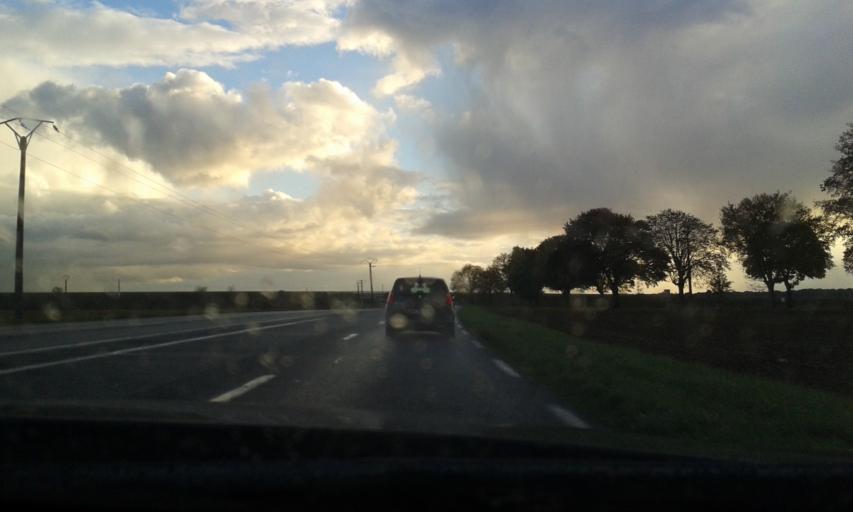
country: FR
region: Centre
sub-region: Departement du Loiret
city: Chevilly
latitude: 48.0484
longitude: 1.8753
